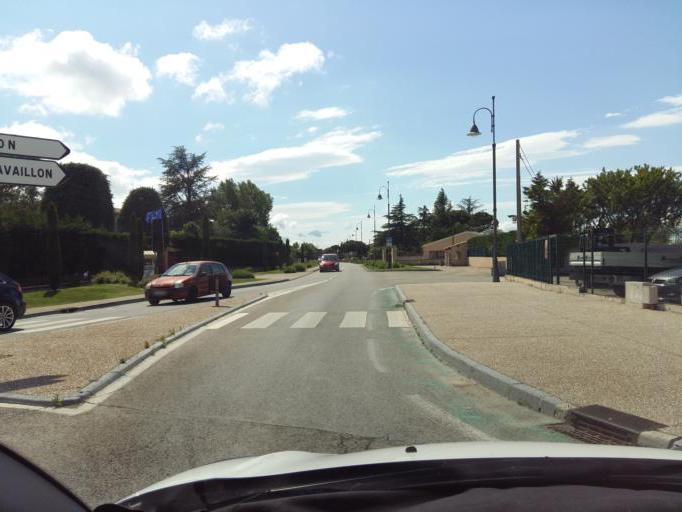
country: FR
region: Provence-Alpes-Cote d'Azur
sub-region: Departement du Vaucluse
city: Robion
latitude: 43.8499
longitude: 5.1215
